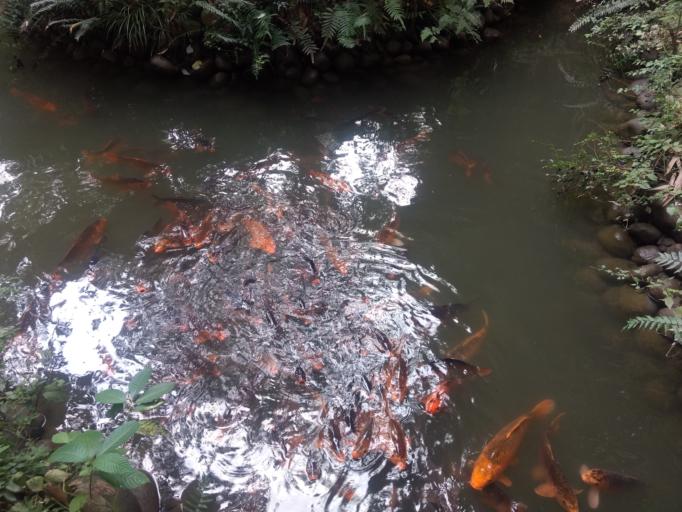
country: CN
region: Sichuan
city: Chengdu
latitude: 30.6619
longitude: 104.0277
